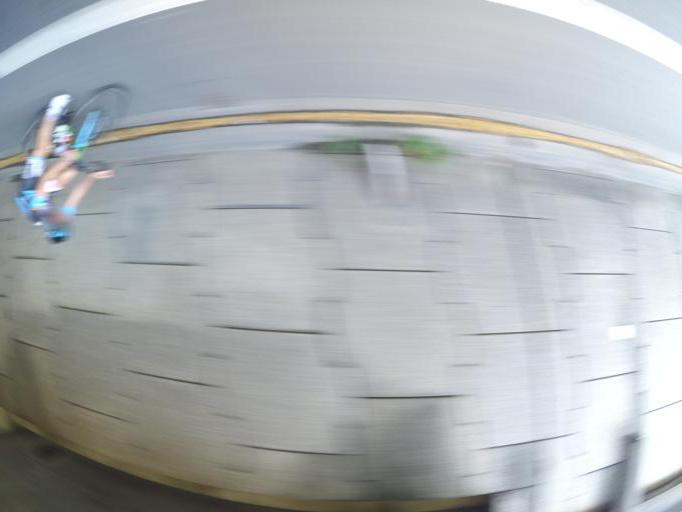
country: FR
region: Pays de la Loire
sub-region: Departement de la Loire-Atlantique
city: Reze
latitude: 47.1888
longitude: -1.5246
